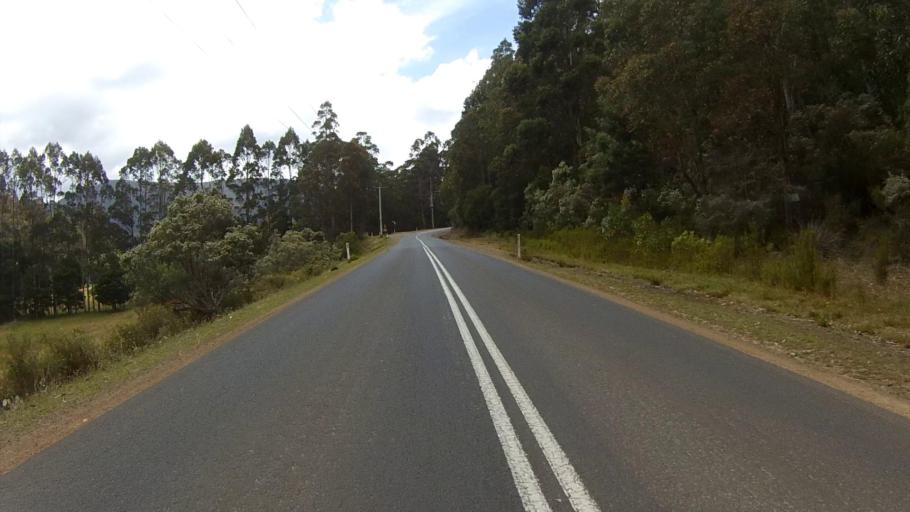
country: AU
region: Tasmania
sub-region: Huon Valley
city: Cygnet
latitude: -43.1321
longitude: 147.1565
